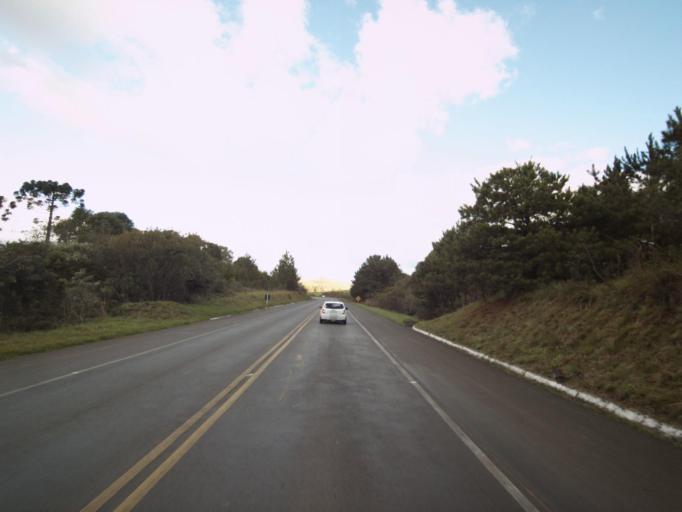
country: BR
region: Santa Catarina
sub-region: Campos Novos
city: Campos Novos
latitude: -27.3255
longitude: -51.3600
